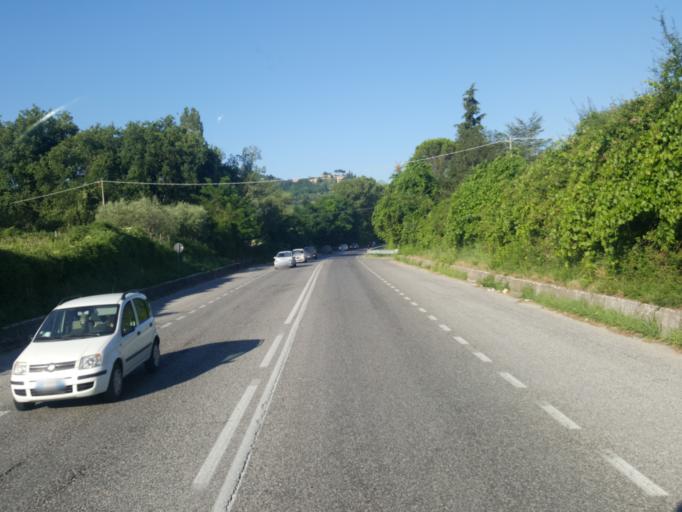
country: IT
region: The Marches
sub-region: Provincia di Pesaro e Urbino
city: Borgo Santa Maria
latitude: 43.8561
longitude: 12.8087
